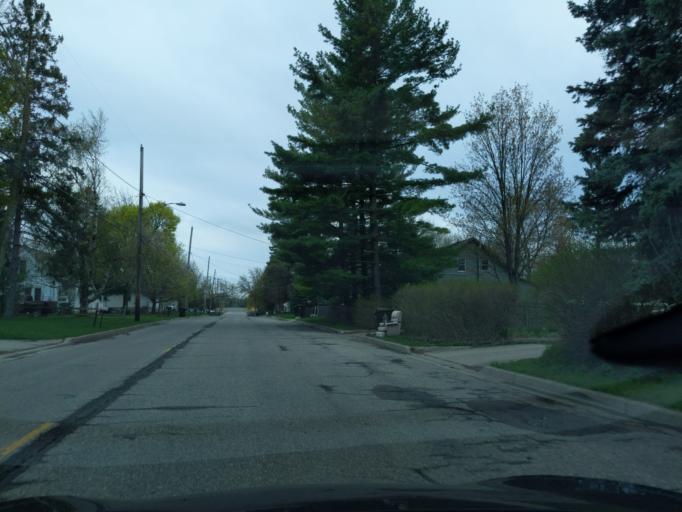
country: US
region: Michigan
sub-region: Ingham County
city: Edgemont Park
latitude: 42.7293
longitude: -84.5877
